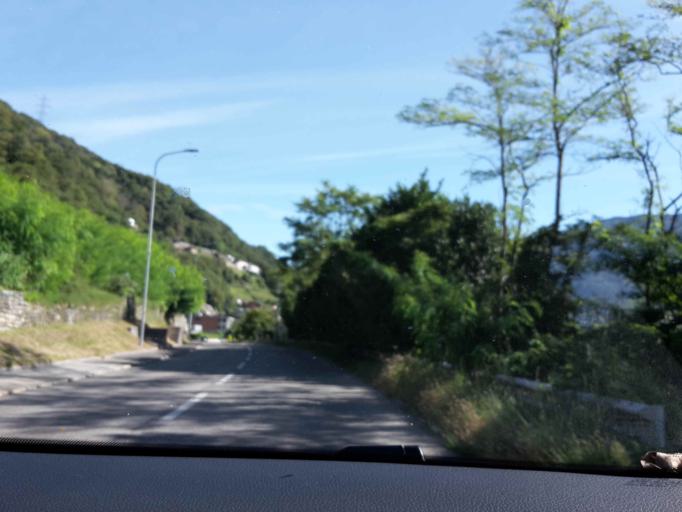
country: CH
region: Ticino
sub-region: Bellinzona District
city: Sementina
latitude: 46.1818
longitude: 8.9804
